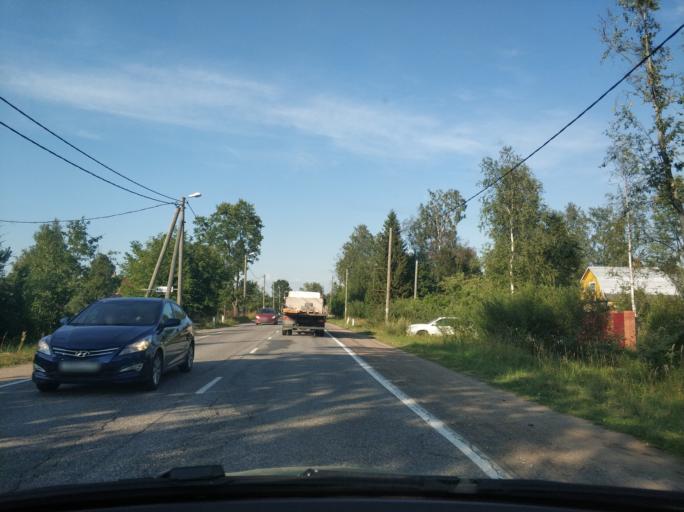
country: RU
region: Leningrad
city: Borisova Griva
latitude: 60.0933
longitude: 30.9626
